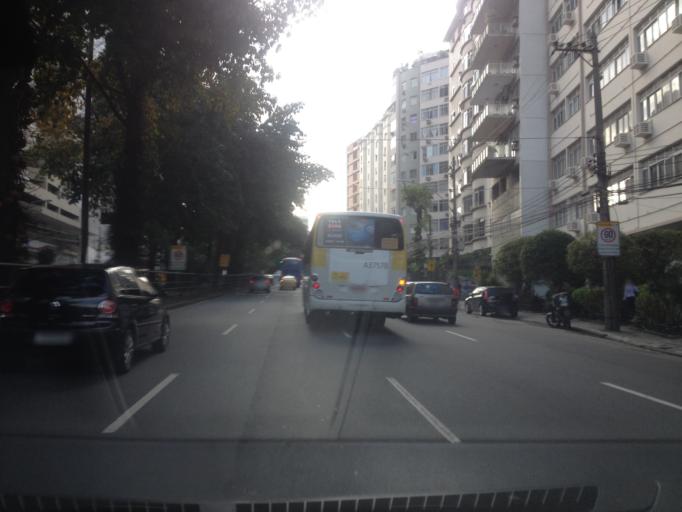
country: BR
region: Rio de Janeiro
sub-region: Rio De Janeiro
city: Rio de Janeiro
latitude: -22.9600
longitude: -43.2021
